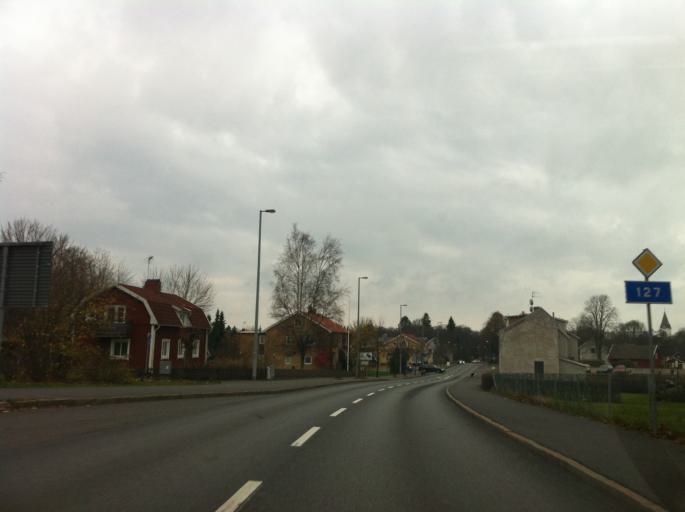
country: SE
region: Joenkoeping
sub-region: Savsjo Kommun
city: Stockaryd
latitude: 57.3746
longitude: 14.5403
